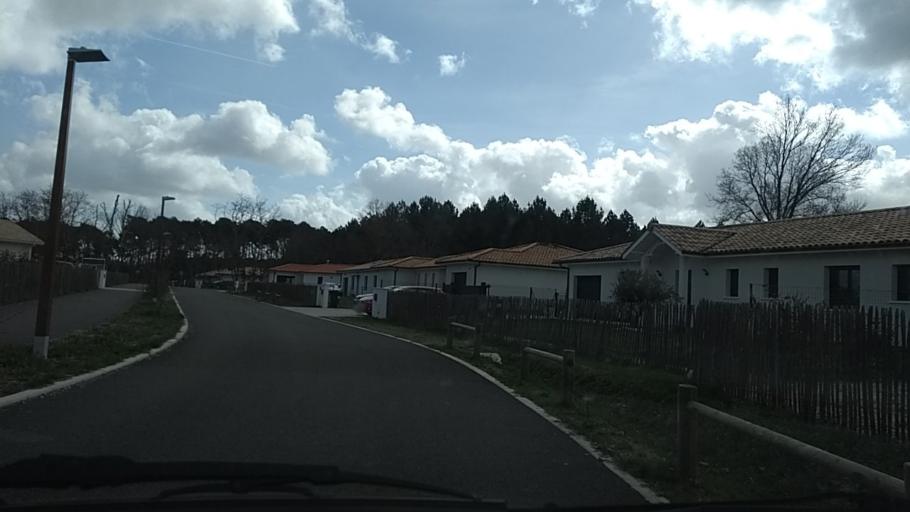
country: FR
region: Aquitaine
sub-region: Departement de la Gironde
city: Salles
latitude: 44.5469
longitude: -0.8774
